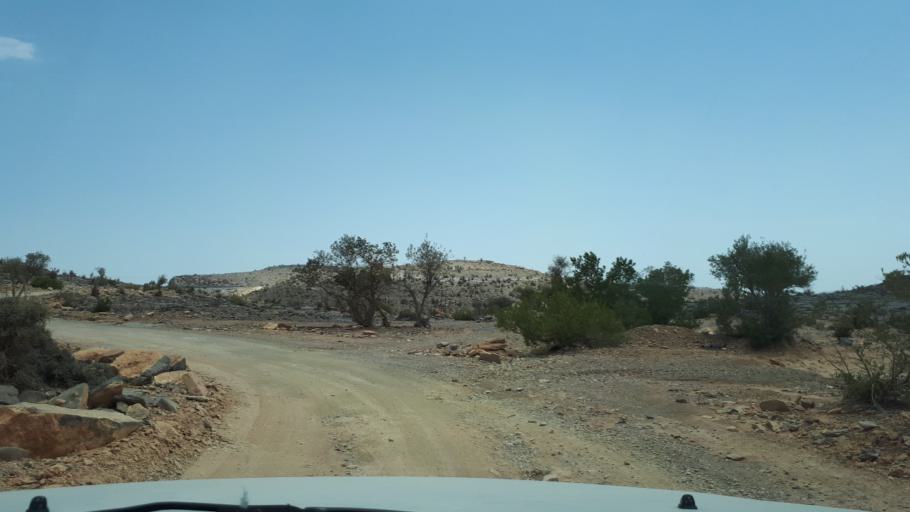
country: OM
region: Muhafazat ad Dakhiliyah
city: Bahla'
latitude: 23.2066
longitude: 57.1986
